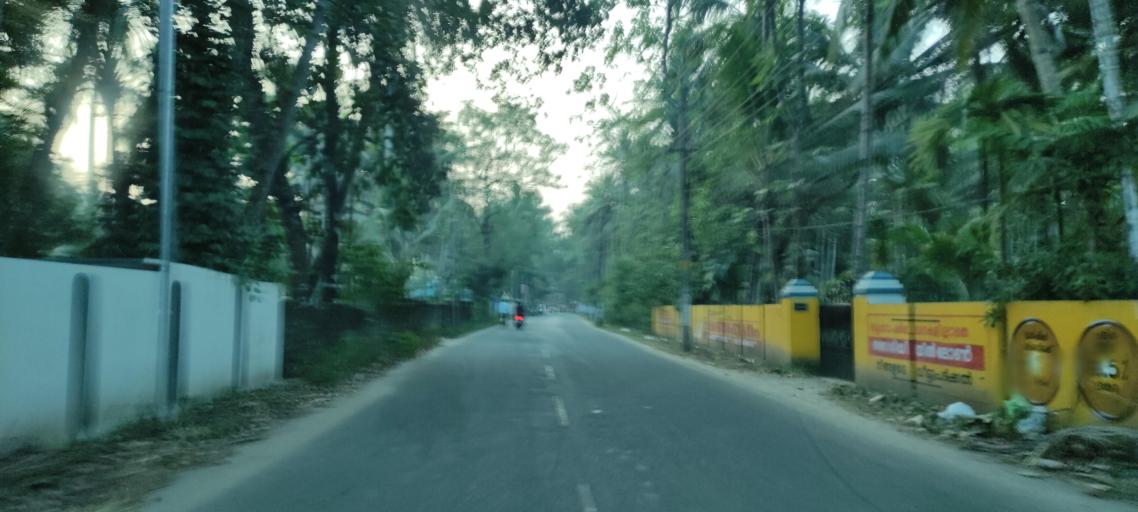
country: IN
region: Kerala
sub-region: Alappuzha
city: Kayankulam
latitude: 9.1252
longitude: 76.4978
